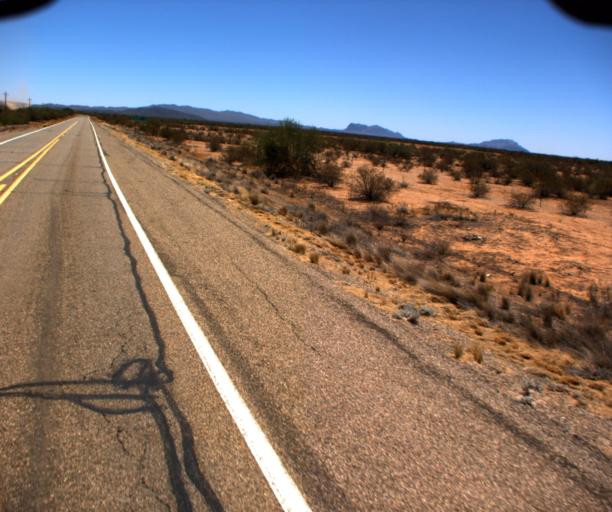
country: US
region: Arizona
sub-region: Pima County
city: Ajo
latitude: 32.1834
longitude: -112.3549
